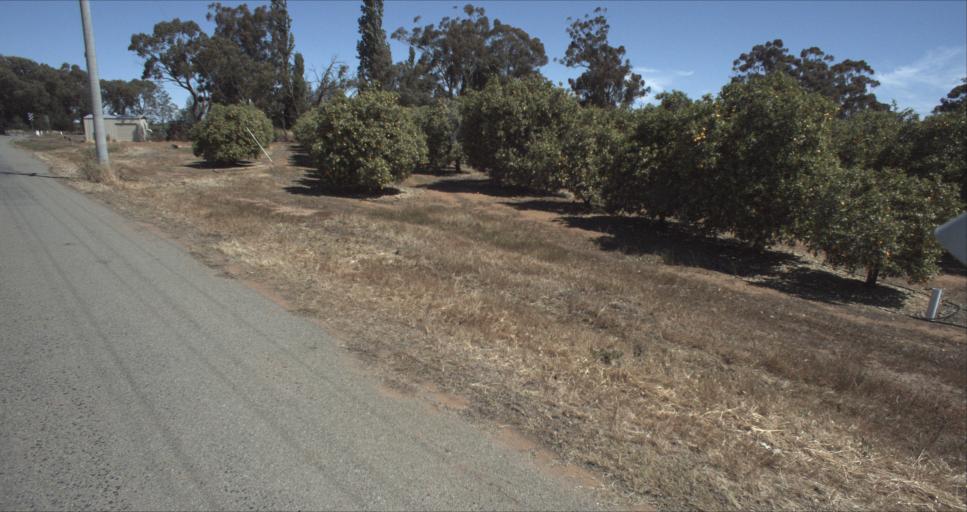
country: AU
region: New South Wales
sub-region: Leeton
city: Leeton
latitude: -34.5439
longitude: 146.3534
